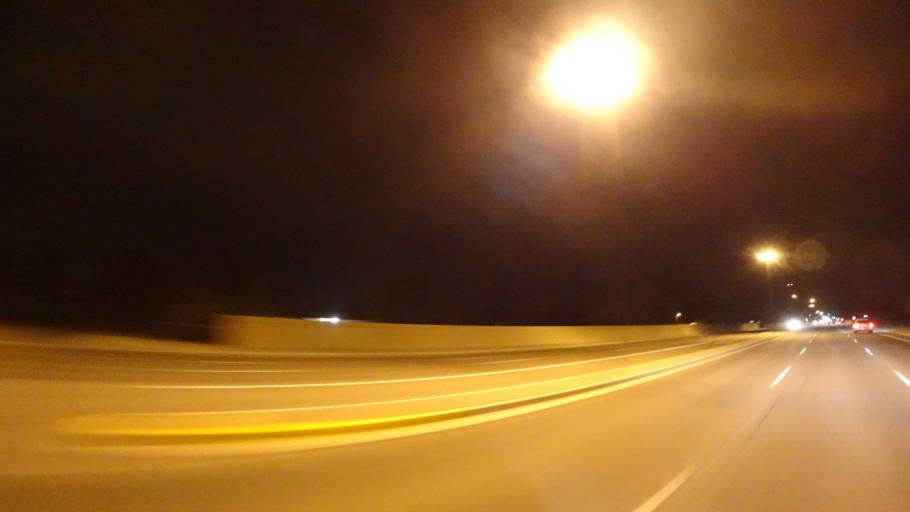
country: US
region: Arizona
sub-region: Maricopa County
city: Gilbert
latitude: 33.3629
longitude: -111.7218
